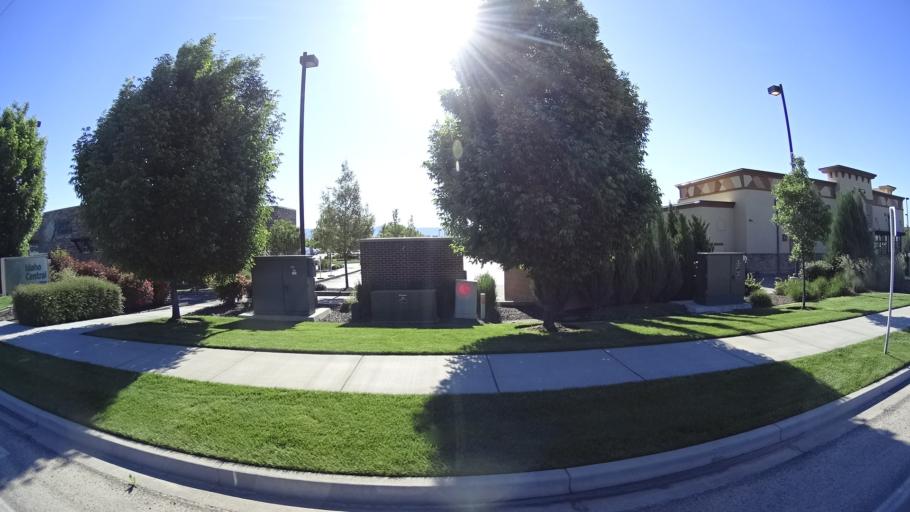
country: US
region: Idaho
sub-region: Ada County
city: Meridian
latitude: 43.6644
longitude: -116.4136
